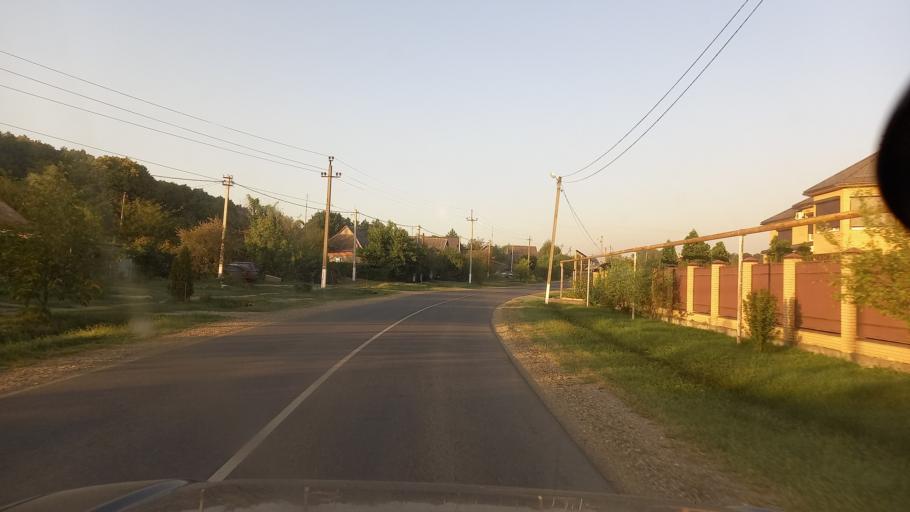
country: RU
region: Krasnodarskiy
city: Smolenskaya
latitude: 44.7680
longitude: 38.7798
